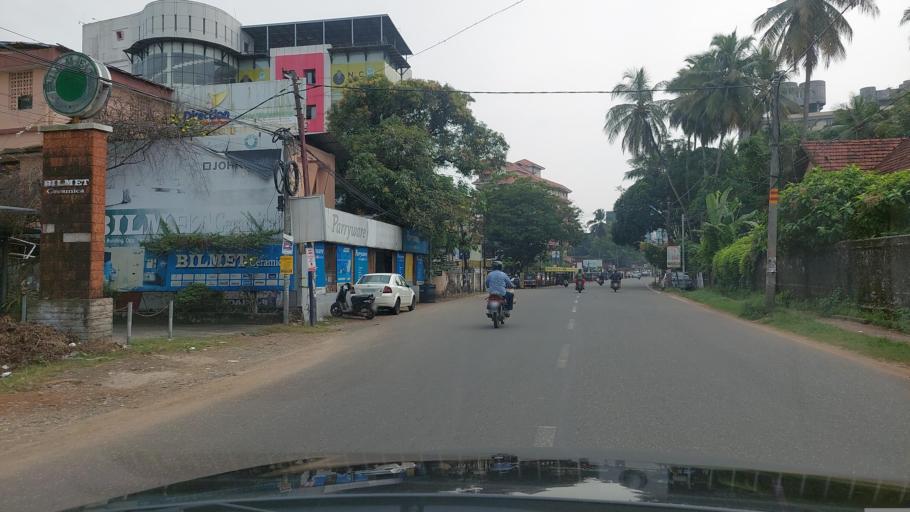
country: IN
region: Kerala
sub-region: Kozhikode
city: Kozhikode
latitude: 11.2635
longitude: 75.7802
